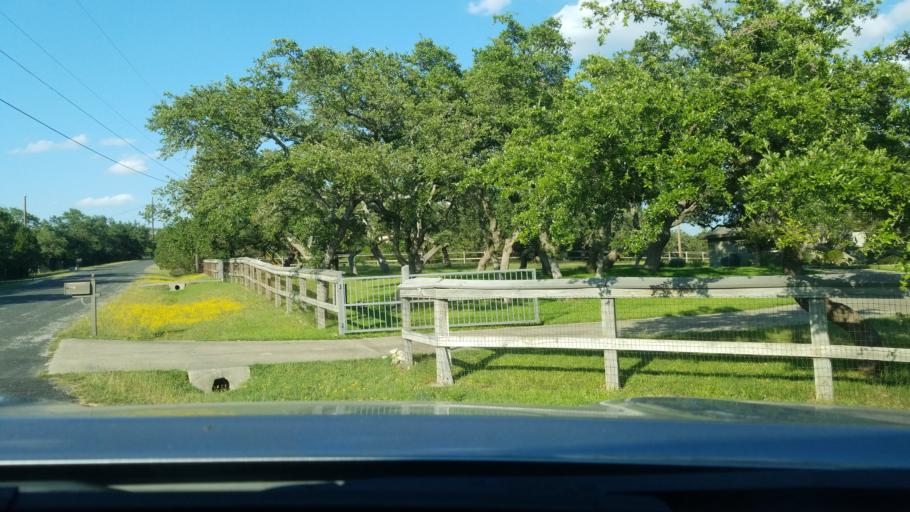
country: US
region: Texas
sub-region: Bexar County
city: Timberwood Park
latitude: 29.6998
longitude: -98.4408
